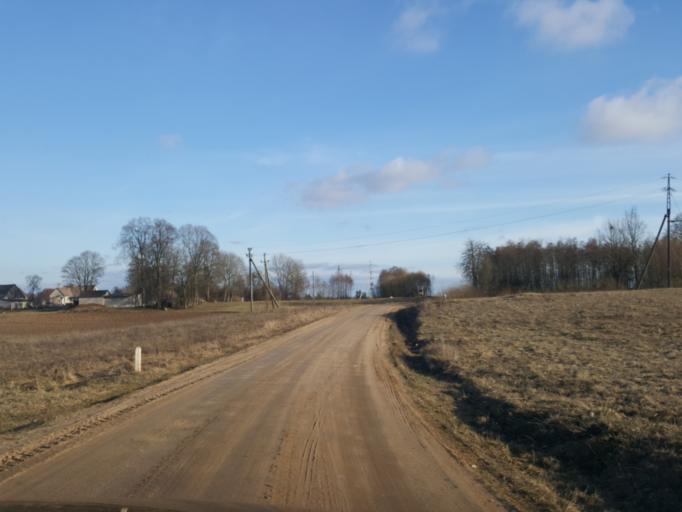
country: LT
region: Alytaus apskritis
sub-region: Alytus
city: Alytus
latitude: 54.3425
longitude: 23.8696
